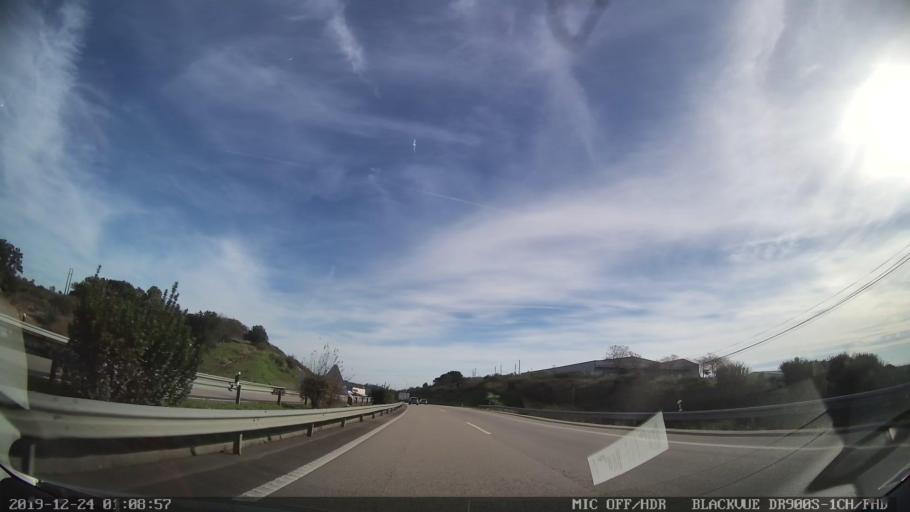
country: PT
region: Santarem
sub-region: Torres Novas
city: Torres Novas
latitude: 39.4641
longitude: -8.5367
